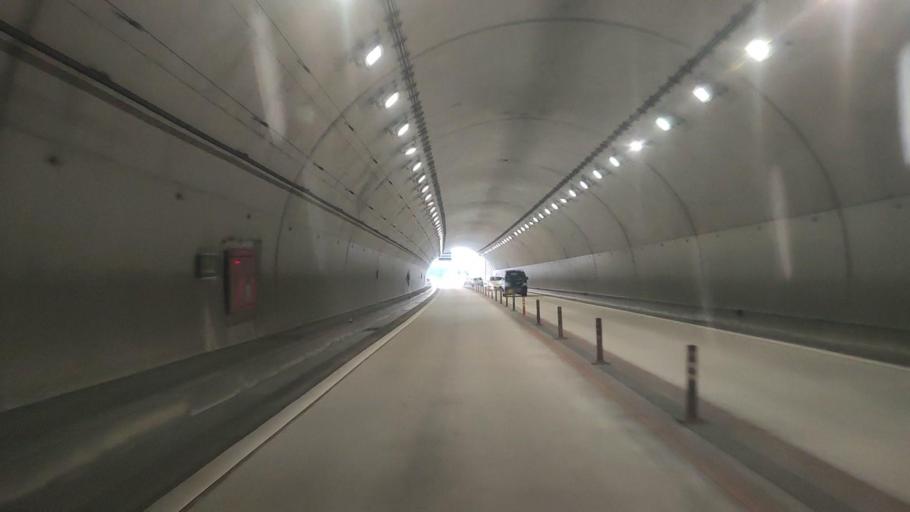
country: JP
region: Nagasaki
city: Shimabara
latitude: 32.7719
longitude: 130.3574
